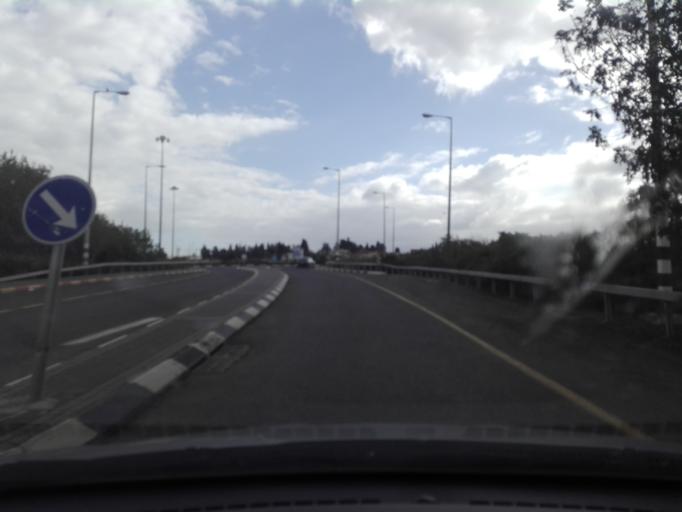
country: IL
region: Haifa
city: Daliyat el Karmil
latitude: 32.6370
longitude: 35.0634
